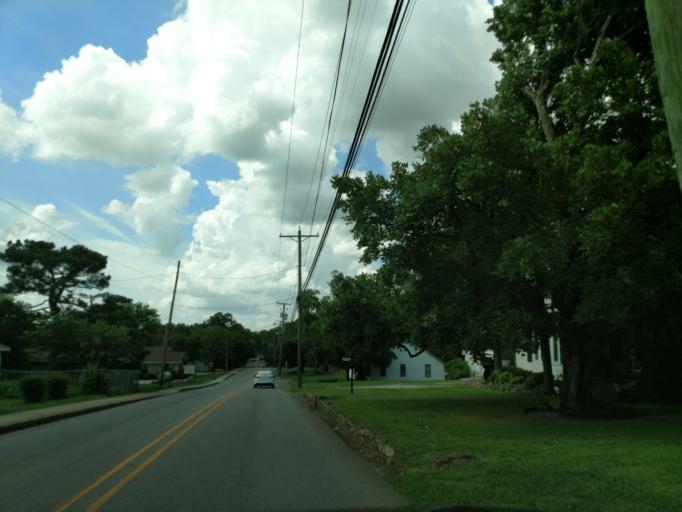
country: US
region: Arkansas
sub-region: Carroll County
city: Berryville
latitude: 36.3656
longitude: -93.5663
